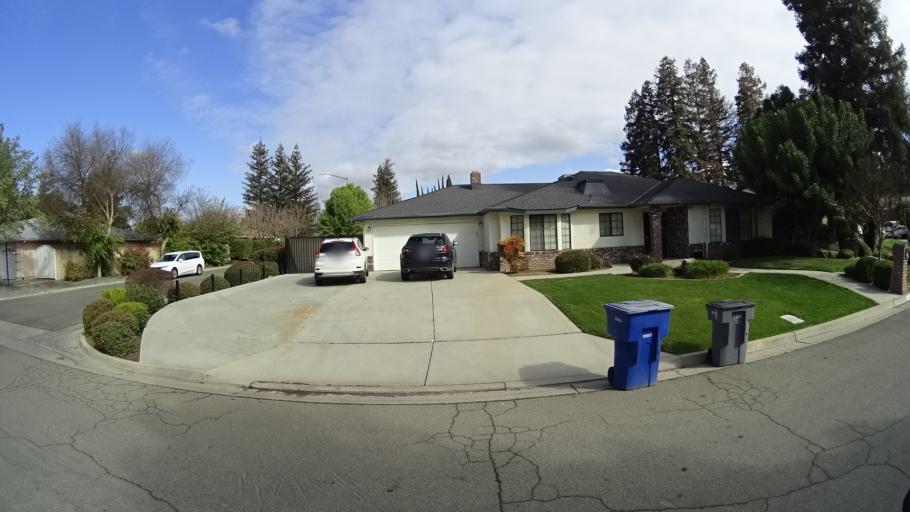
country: US
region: California
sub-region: Fresno County
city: Fresno
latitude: 36.8328
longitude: -119.8577
